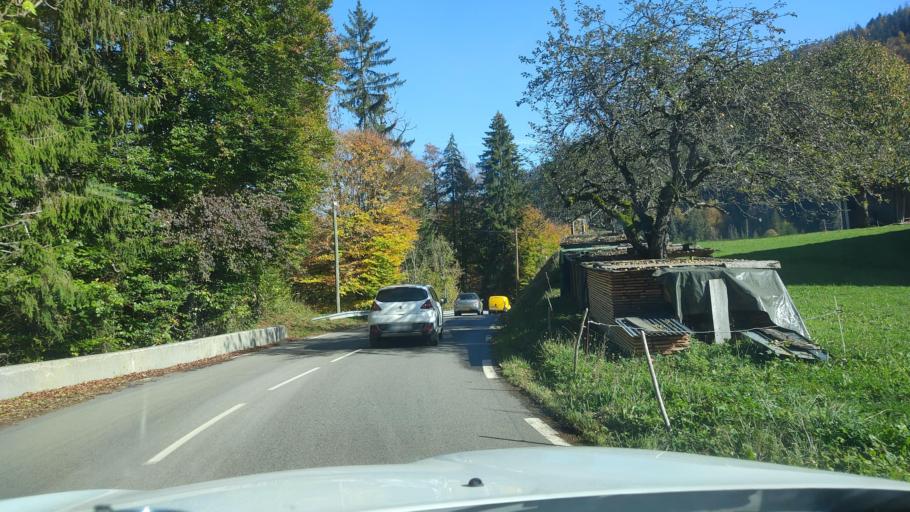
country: FR
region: Rhone-Alpes
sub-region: Departement de la Savoie
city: Ugine
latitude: 45.7938
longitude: 6.4838
